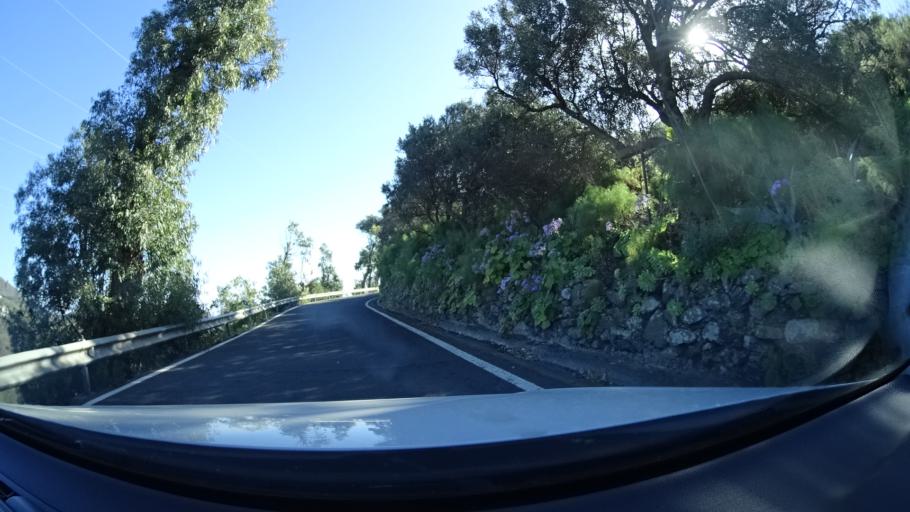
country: ES
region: Canary Islands
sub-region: Provincia de Las Palmas
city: Santa Brigida
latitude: 28.0185
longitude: -15.4623
